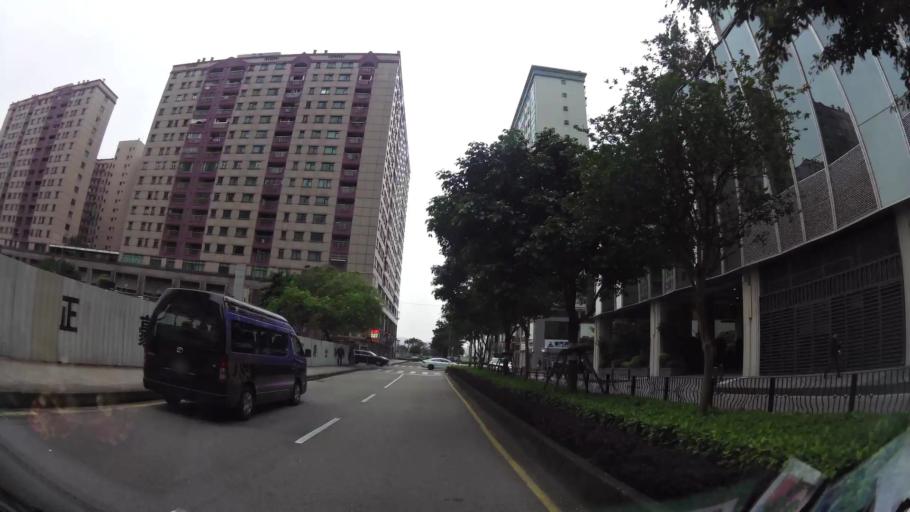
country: MO
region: Macau
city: Macau
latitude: 22.1881
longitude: 113.5490
